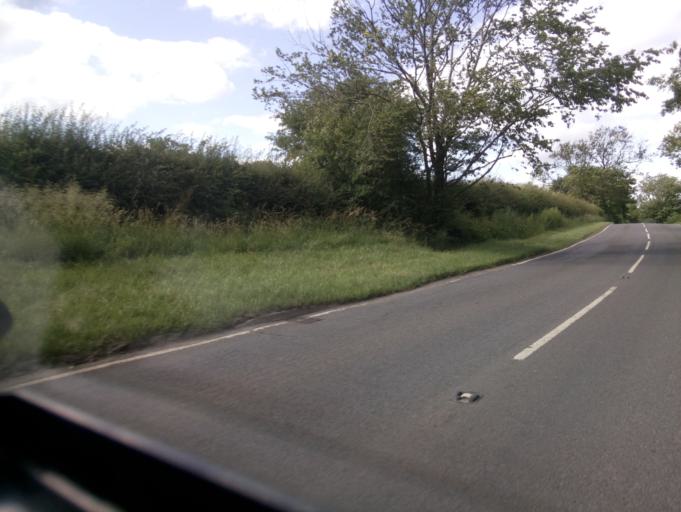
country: GB
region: England
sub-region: Leicestershire
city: Coalville
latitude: 52.7543
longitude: -1.4148
